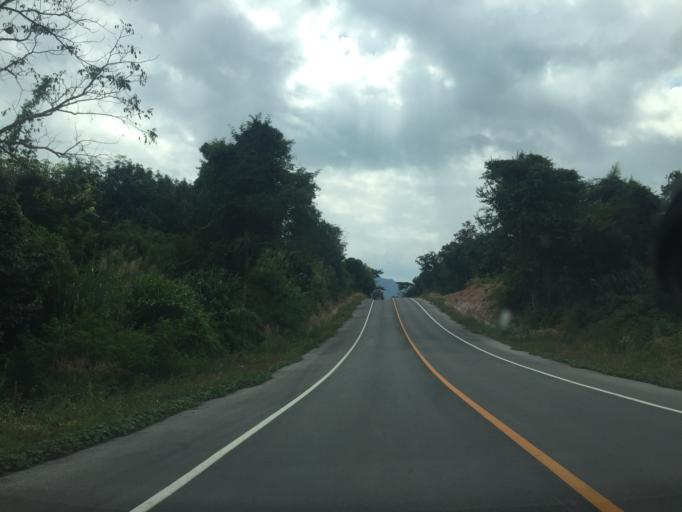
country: TH
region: Lampang
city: Mueang Pan
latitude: 18.8035
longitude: 99.5140
